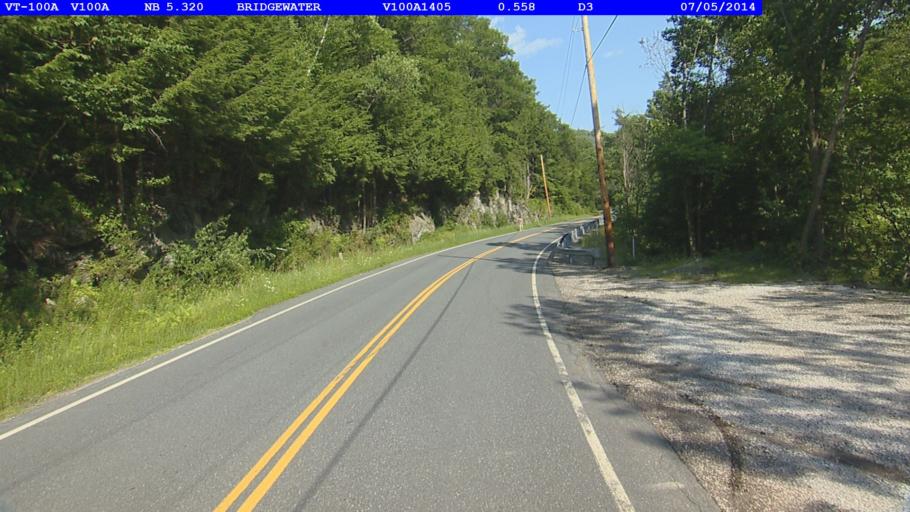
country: US
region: Vermont
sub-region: Windsor County
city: Woodstock
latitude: 43.5728
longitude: -72.6717
